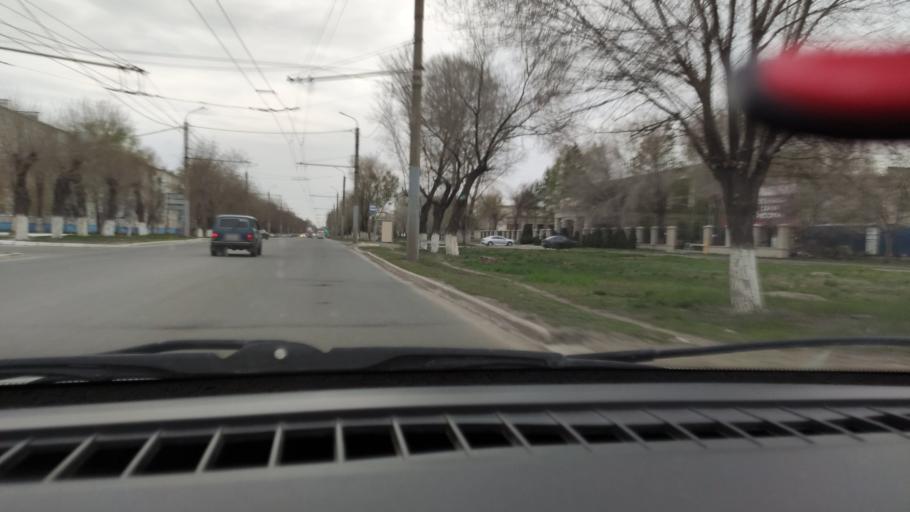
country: RU
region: Orenburg
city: Orenburg
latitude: 51.8440
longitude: 55.1315
